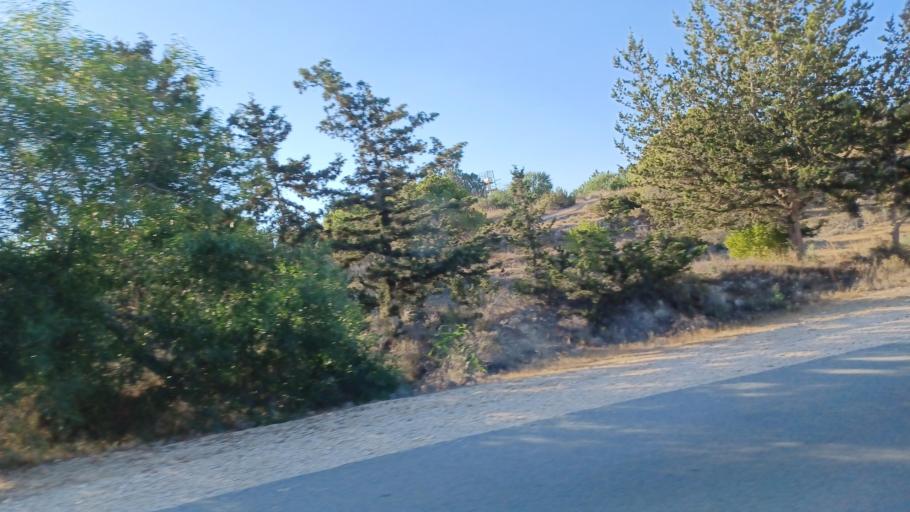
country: CY
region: Larnaka
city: Xylotymbou
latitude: 34.9880
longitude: 33.7429
